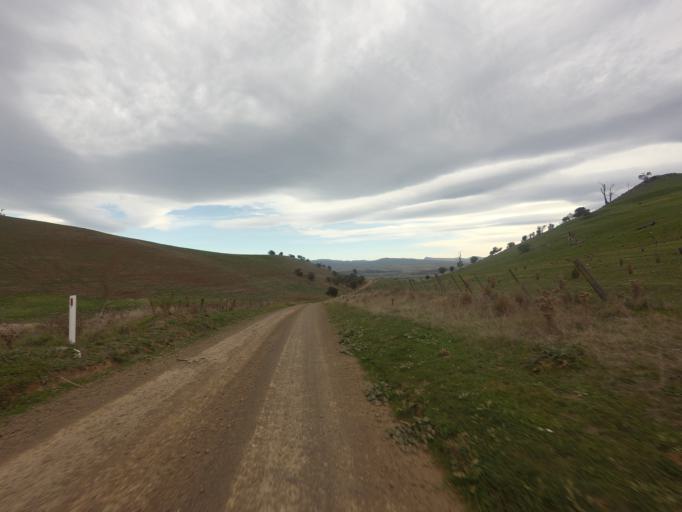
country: AU
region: Tasmania
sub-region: Derwent Valley
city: New Norfolk
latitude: -42.4537
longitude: 146.7692
